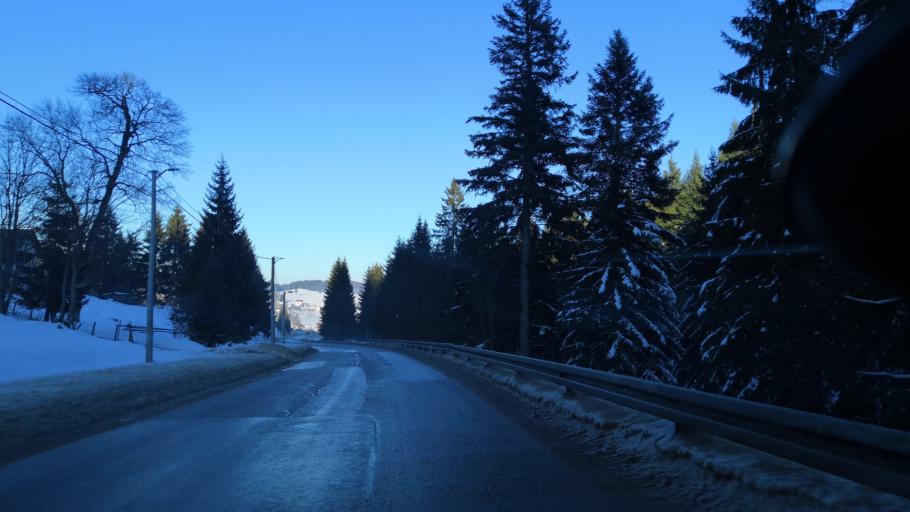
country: BA
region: Republika Srpska
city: Han Pijesak
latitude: 44.0884
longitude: 18.9531
